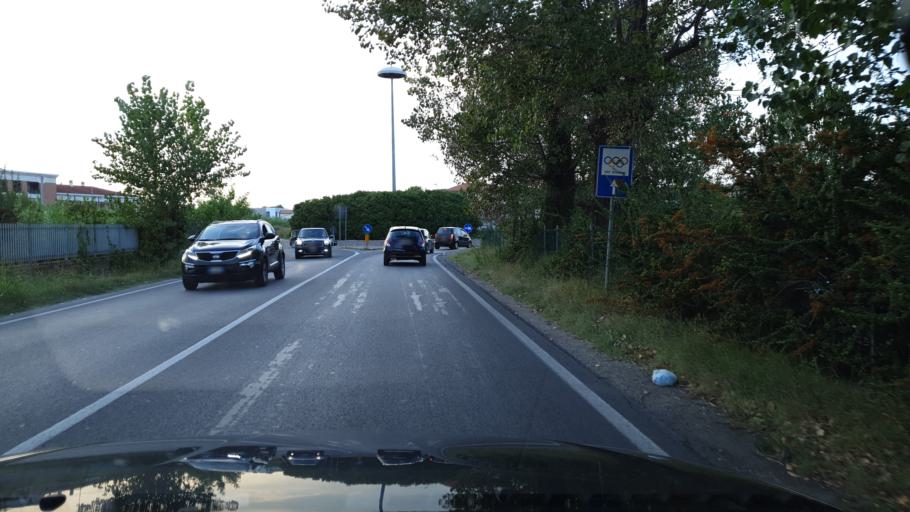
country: IT
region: Emilia-Romagna
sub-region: Provincia di Rimini
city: Rivazzurra
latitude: 44.0366
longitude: 12.5987
